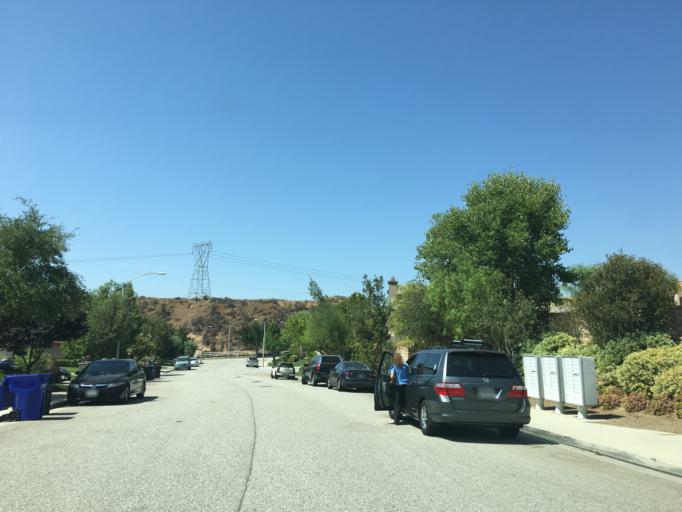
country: US
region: California
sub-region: Los Angeles County
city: Valencia
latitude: 34.4688
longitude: -118.5639
